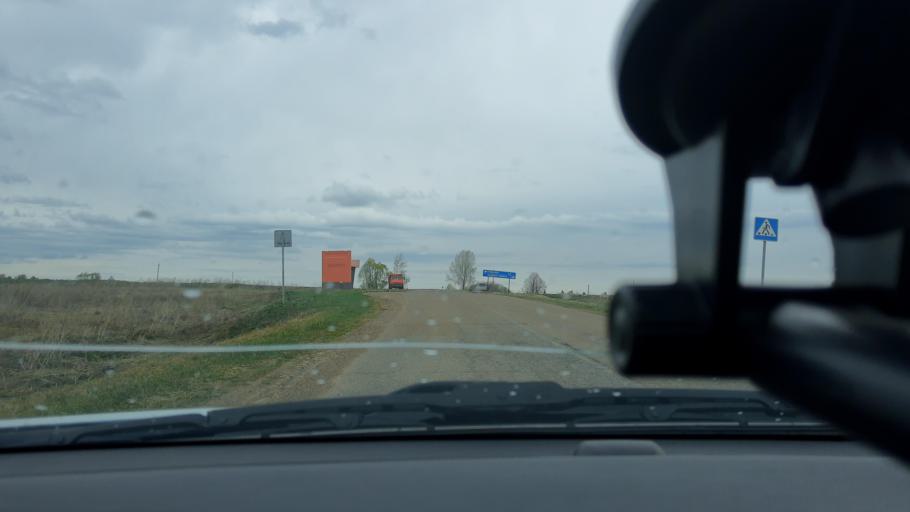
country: RU
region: Bashkortostan
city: Pavlovka
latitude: 55.3209
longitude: 56.3485
